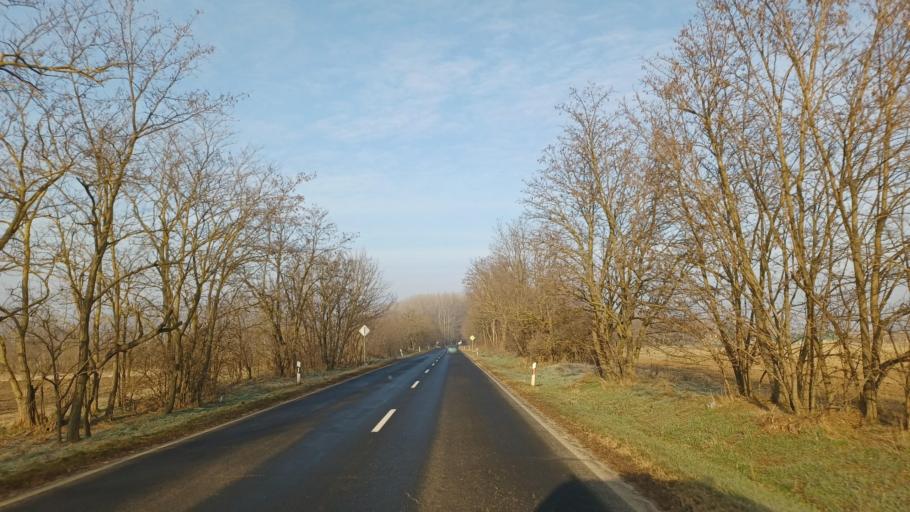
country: HU
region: Fejer
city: Cece
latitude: 46.7437
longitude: 18.6490
